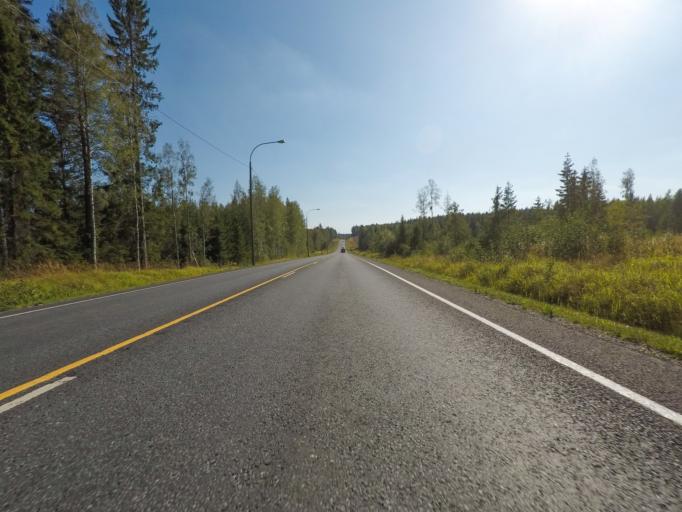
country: FI
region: Northern Savo
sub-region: Varkaus
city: Leppaevirta
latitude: 62.6183
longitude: 27.6223
